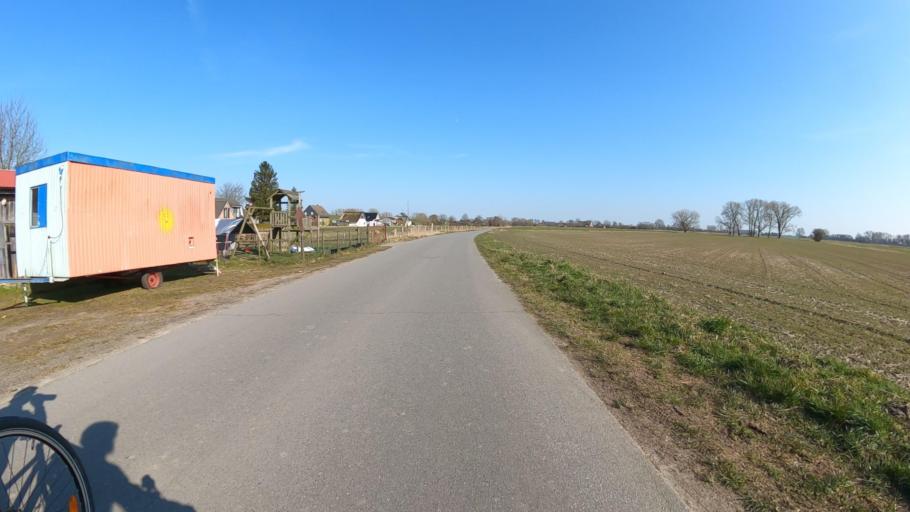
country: DE
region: Schleswig-Holstein
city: Seestermuhe
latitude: 53.7148
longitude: 9.5636
